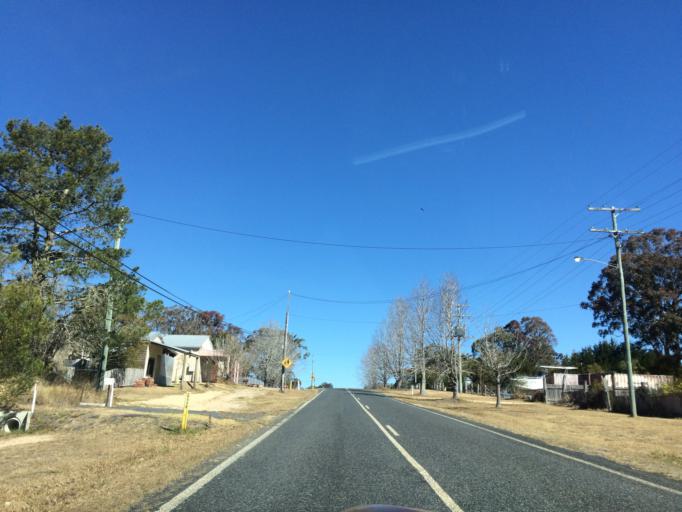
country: AU
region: Queensland
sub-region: Southern Downs
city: Stanthorpe
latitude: -28.6450
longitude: 152.0851
